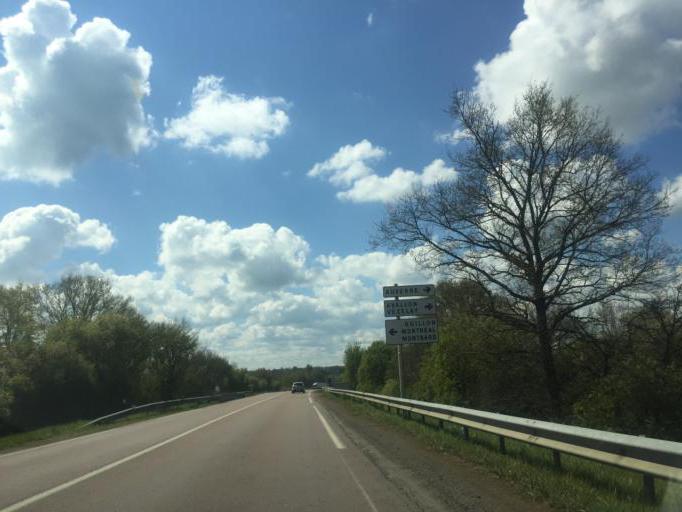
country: FR
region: Bourgogne
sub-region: Departement de l'Yonne
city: Avallon
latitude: 47.5057
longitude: 3.9923
